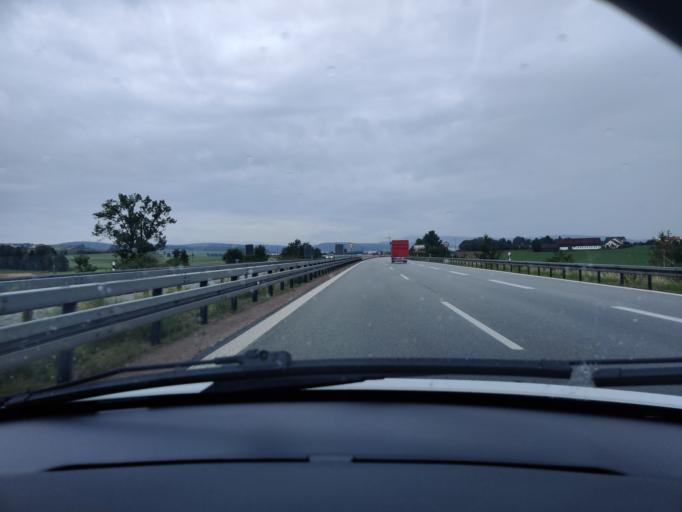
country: DE
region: Bavaria
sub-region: Upper Palatinate
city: Pfreimd
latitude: 49.4723
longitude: 12.1933
